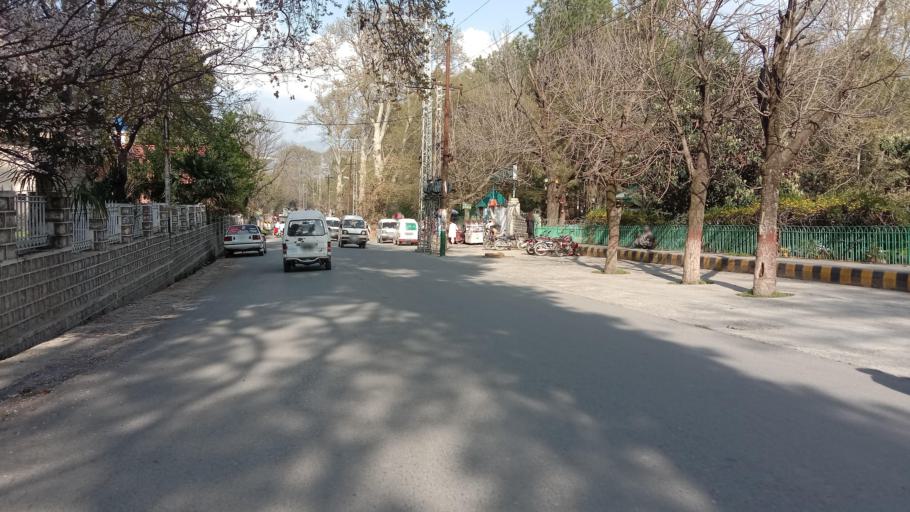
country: PK
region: Khyber Pakhtunkhwa
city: Abbottabad
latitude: 34.1502
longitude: 73.2146
